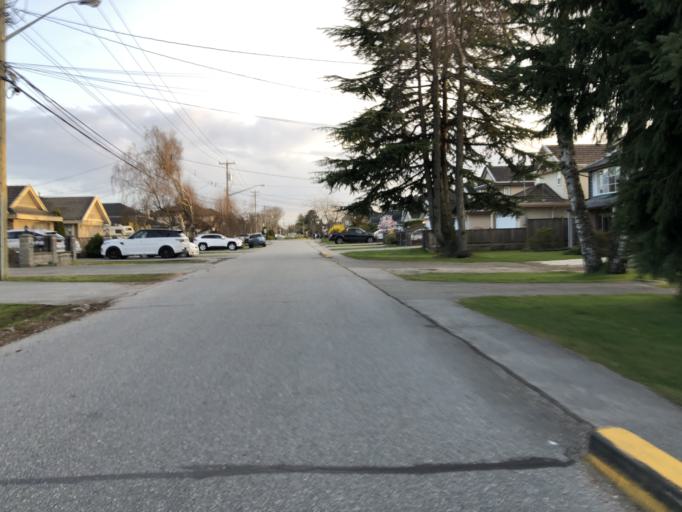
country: CA
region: British Columbia
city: Richmond
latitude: 49.1530
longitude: -123.1226
